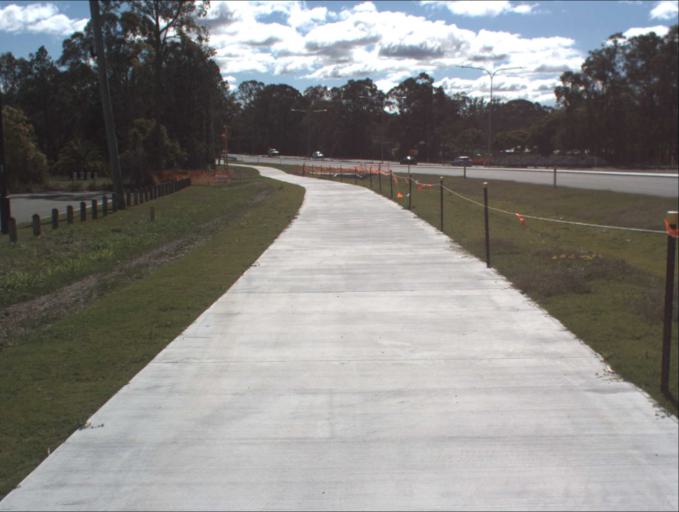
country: AU
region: Queensland
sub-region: Logan
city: Logan Reserve
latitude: -27.6967
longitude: 153.1015
